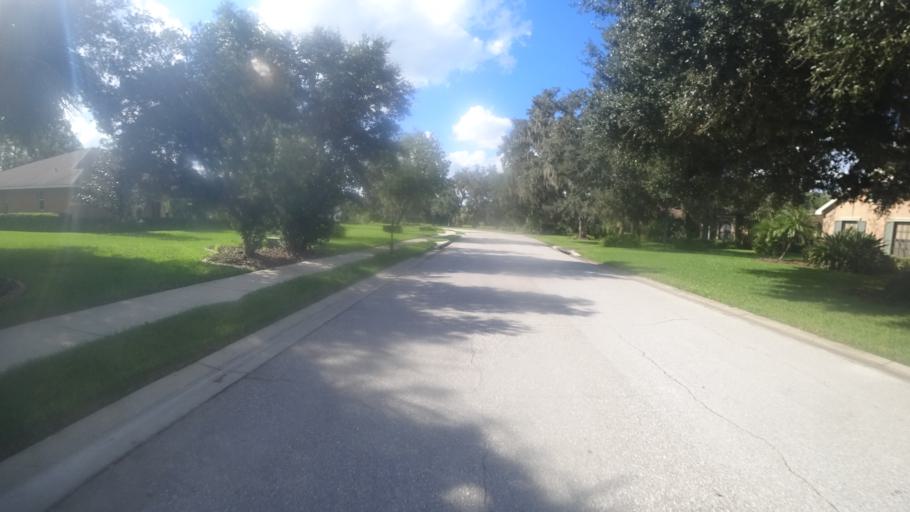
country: US
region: Florida
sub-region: Manatee County
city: Ellenton
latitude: 27.5463
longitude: -82.3837
